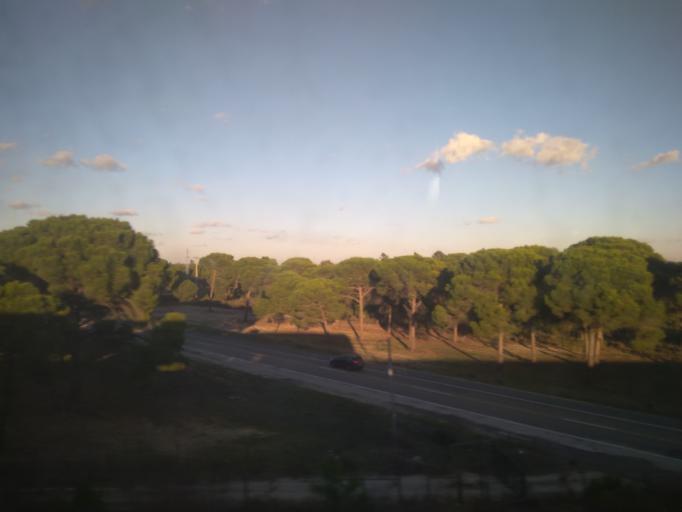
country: PT
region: Setubal
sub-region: Grandola
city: Grandola
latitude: 38.2685
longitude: -8.5429
